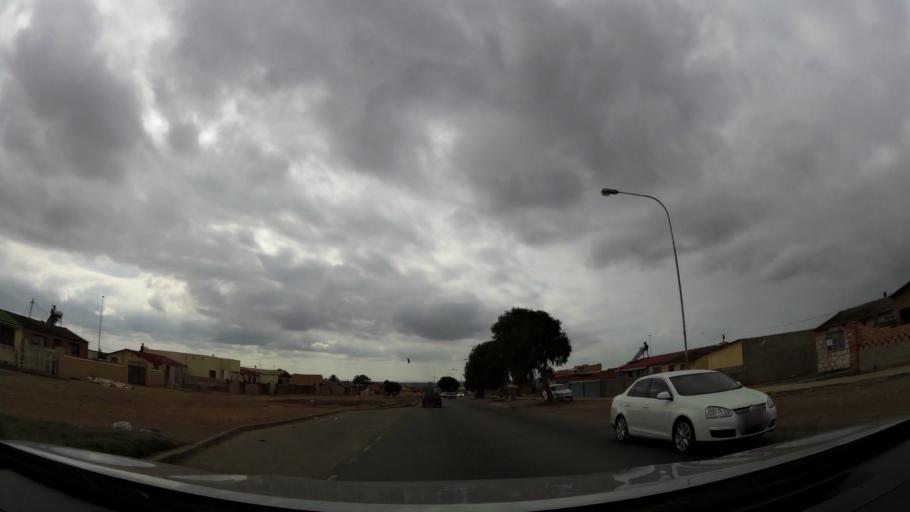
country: ZA
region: Eastern Cape
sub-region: Nelson Mandela Bay Metropolitan Municipality
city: Port Elizabeth
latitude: -33.8738
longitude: 25.5634
